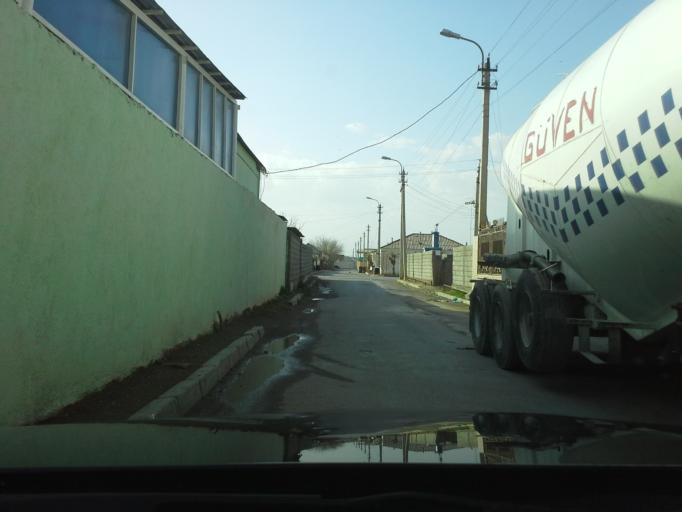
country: TM
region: Ahal
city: Abadan
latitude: 38.0184
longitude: 58.2348
